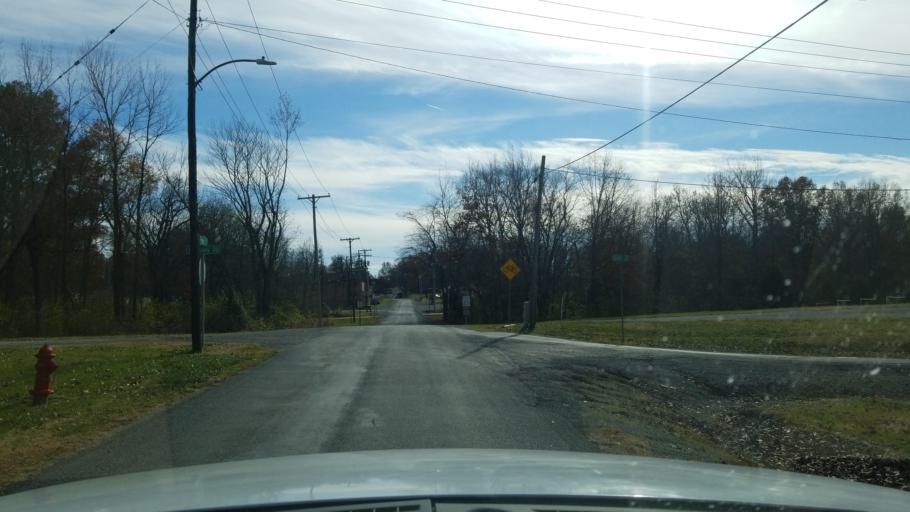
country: US
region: Illinois
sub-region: Saline County
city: Harrisburg
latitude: 37.7665
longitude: -88.5172
